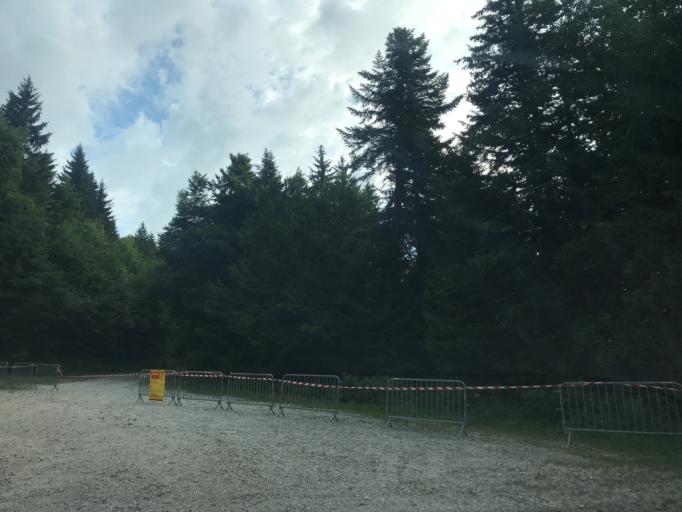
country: FR
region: Rhone-Alpes
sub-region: Departement de l'Isere
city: Barraux
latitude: 45.4207
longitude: 5.9377
